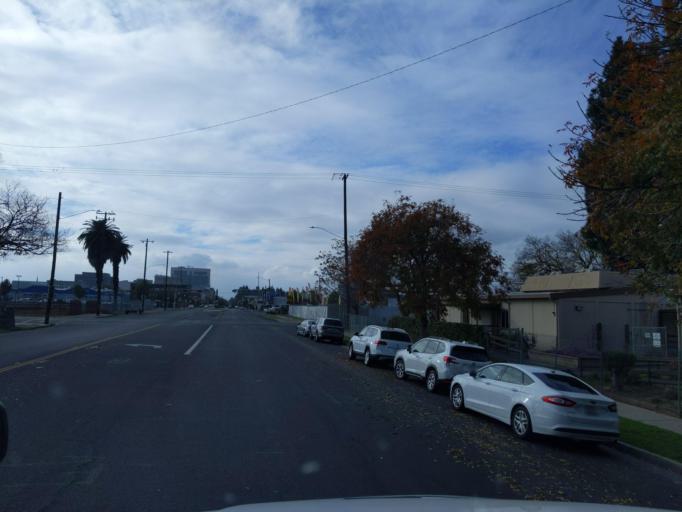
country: US
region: California
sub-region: San Joaquin County
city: Stockton
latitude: 37.9561
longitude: -121.2763
